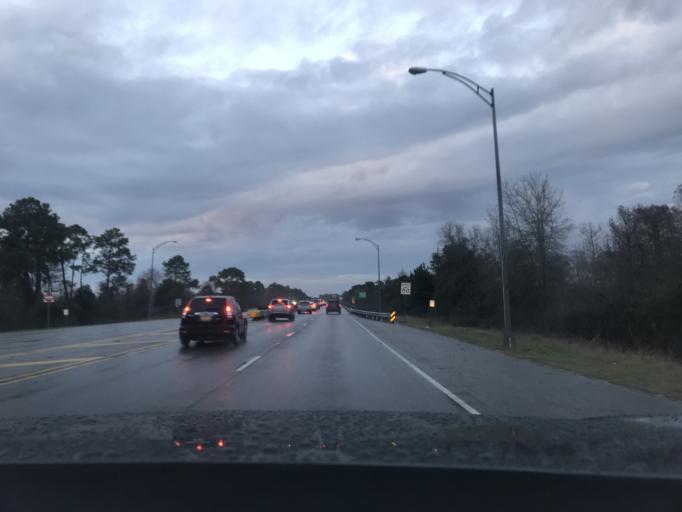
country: US
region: Louisiana
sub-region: Calcasieu Parish
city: Moss Bluff
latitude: 30.2699
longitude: -93.1818
